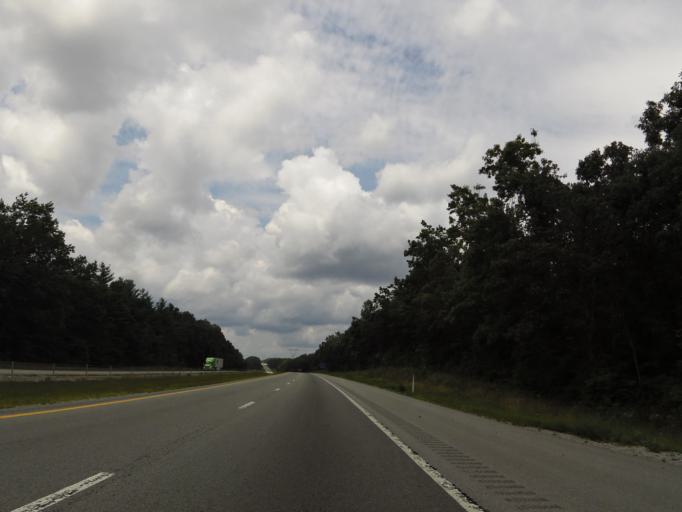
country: US
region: Tennessee
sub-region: Putnam County
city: Monterey
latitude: 36.0690
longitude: -85.1914
